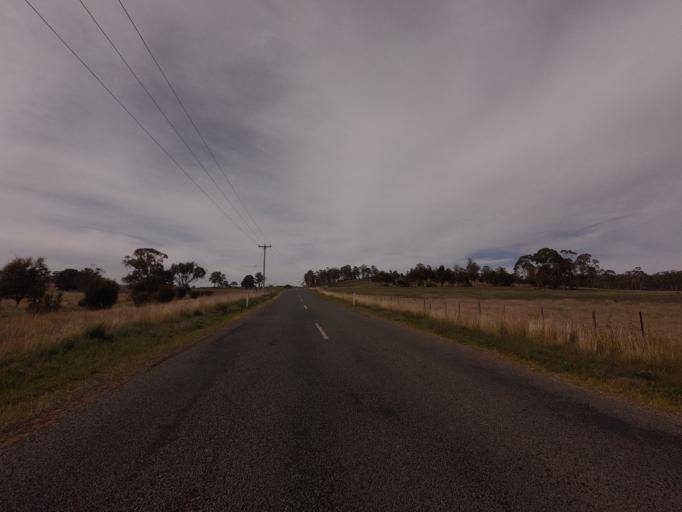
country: AU
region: Tasmania
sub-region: Brighton
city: Bridgewater
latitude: -42.3382
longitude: 147.4026
